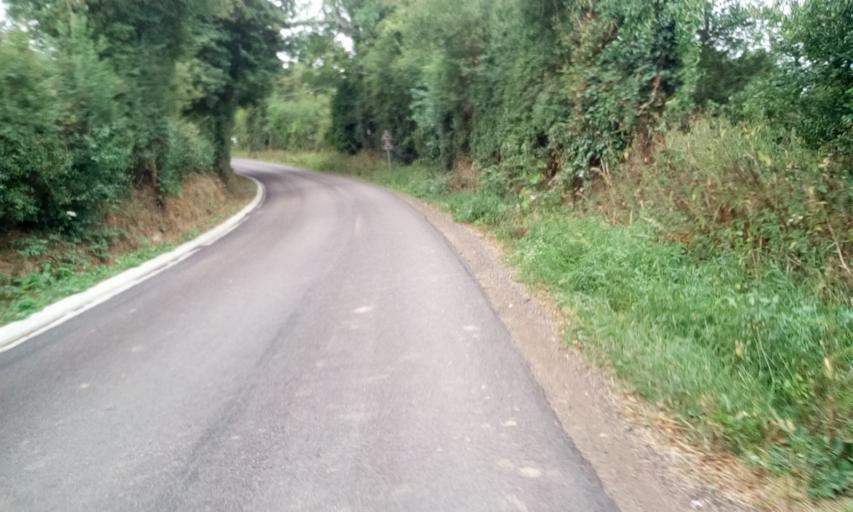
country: FR
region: Lower Normandy
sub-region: Departement du Calvados
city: Troarn
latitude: 49.1914
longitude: -0.1573
